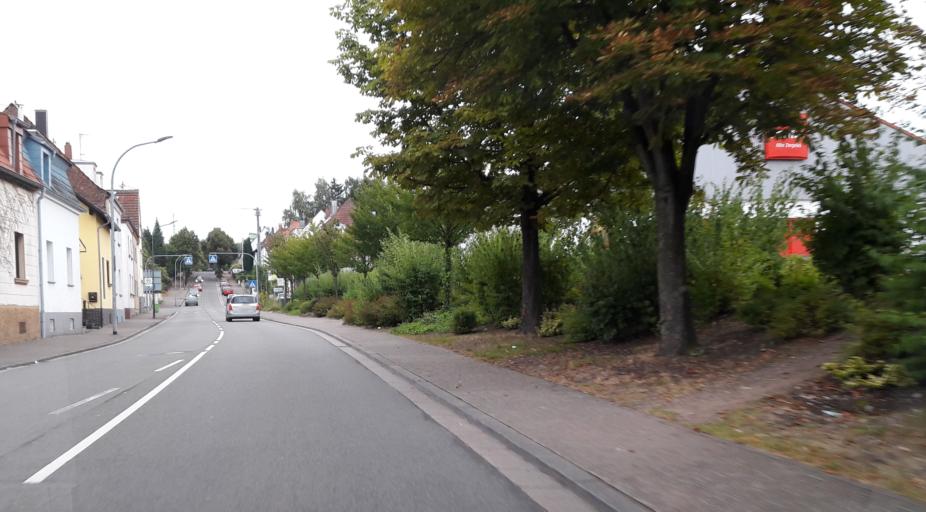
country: DE
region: Saarland
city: Neunkirchen
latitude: 49.3358
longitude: 7.1748
